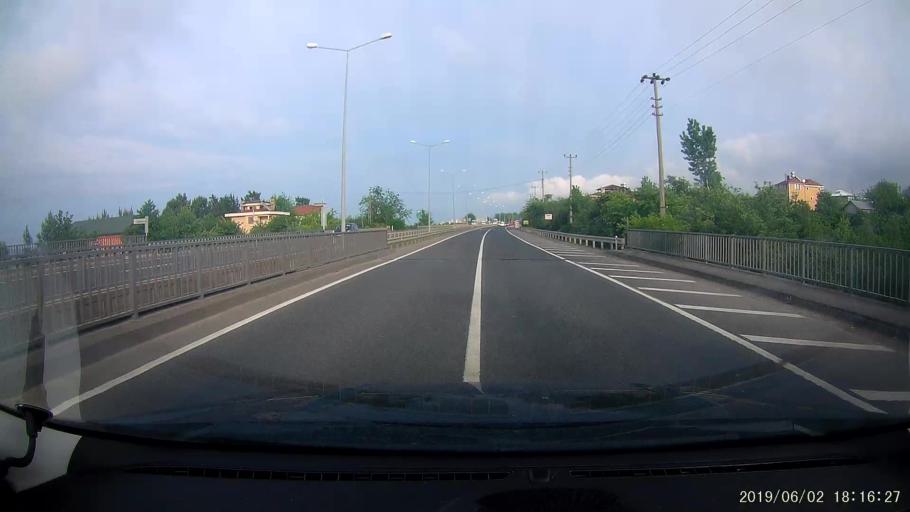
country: TR
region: Ordu
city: Unieh
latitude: 41.1003
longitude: 37.3988
